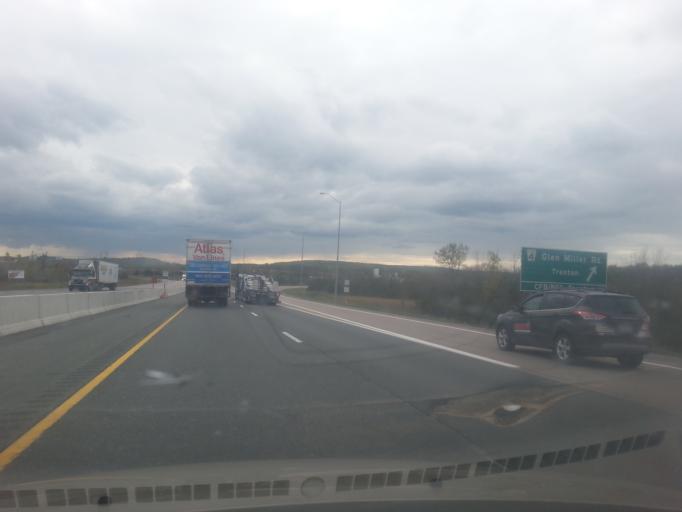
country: CA
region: Ontario
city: Quinte West
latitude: 44.1356
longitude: -77.5765
